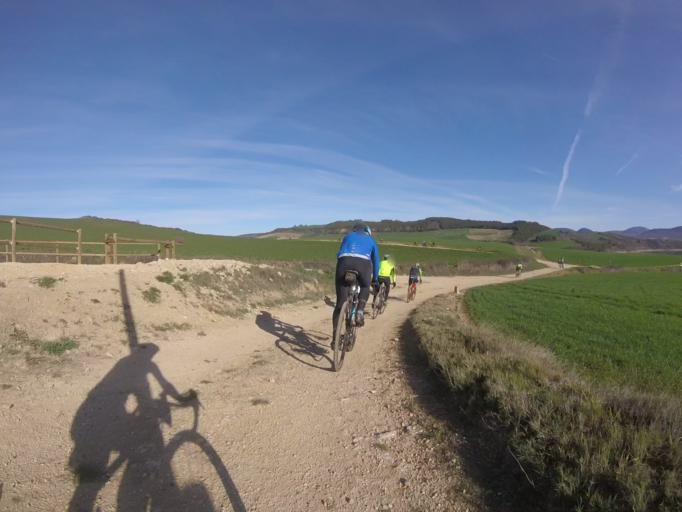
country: ES
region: Navarre
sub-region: Provincia de Navarra
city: Yerri
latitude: 42.7162
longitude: -1.9590
